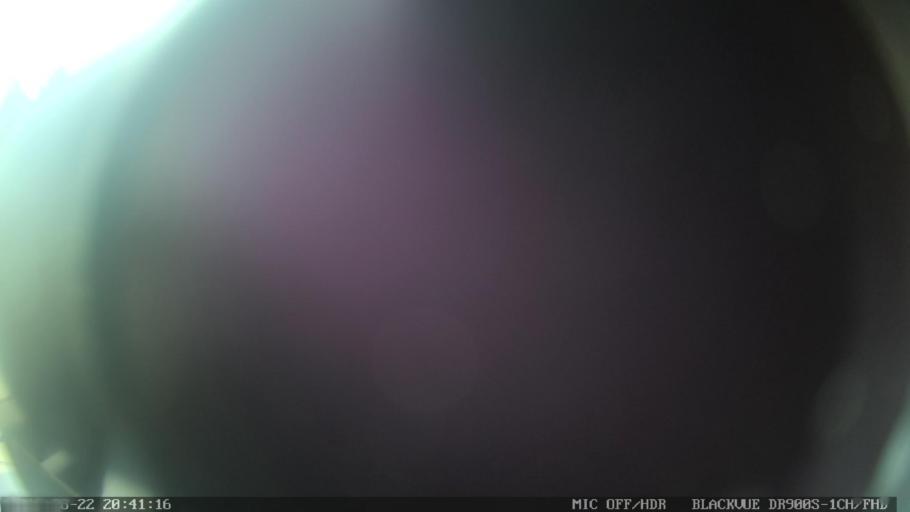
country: PT
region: Castelo Branco
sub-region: Proenca-A-Nova
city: Proenca-a-Nova
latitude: 39.6854
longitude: -7.8019
